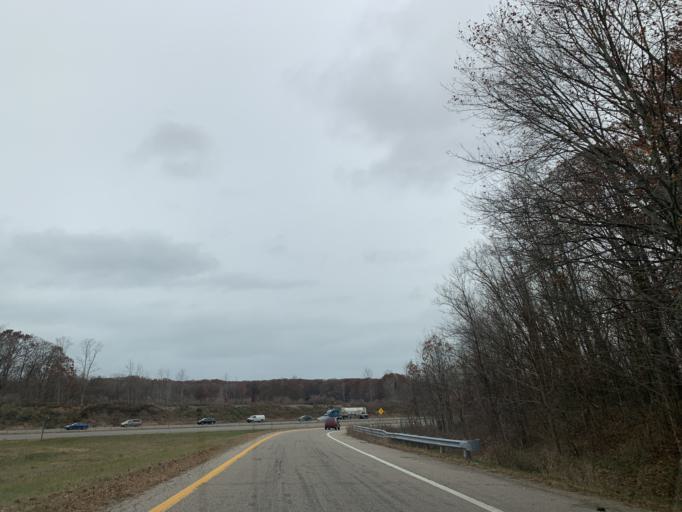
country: US
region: Michigan
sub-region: Berrien County
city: Three Oaks
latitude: 41.8285
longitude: -86.6703
